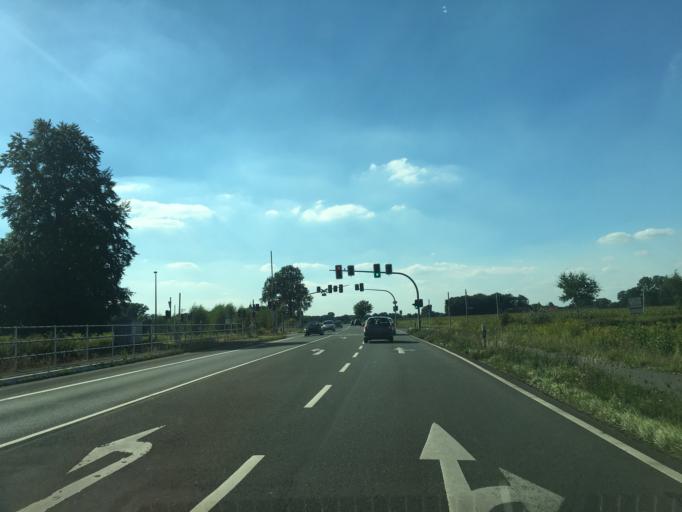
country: DE
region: North Rhine-Westphalia
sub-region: Regierungsbezirk Munster
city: Beelen
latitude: 51.9382
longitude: 8.0837
